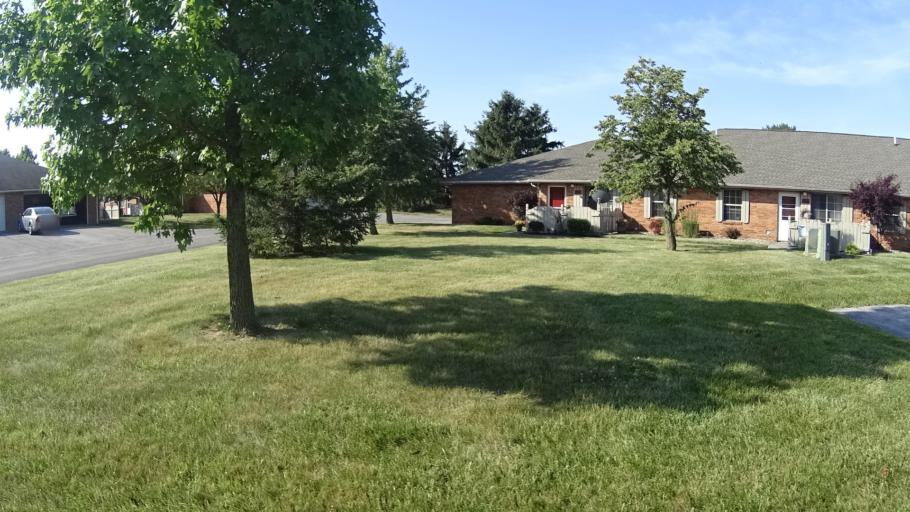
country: US
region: Ohio
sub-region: Erie County
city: Sandusky
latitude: 41.4470
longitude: -82.7851
